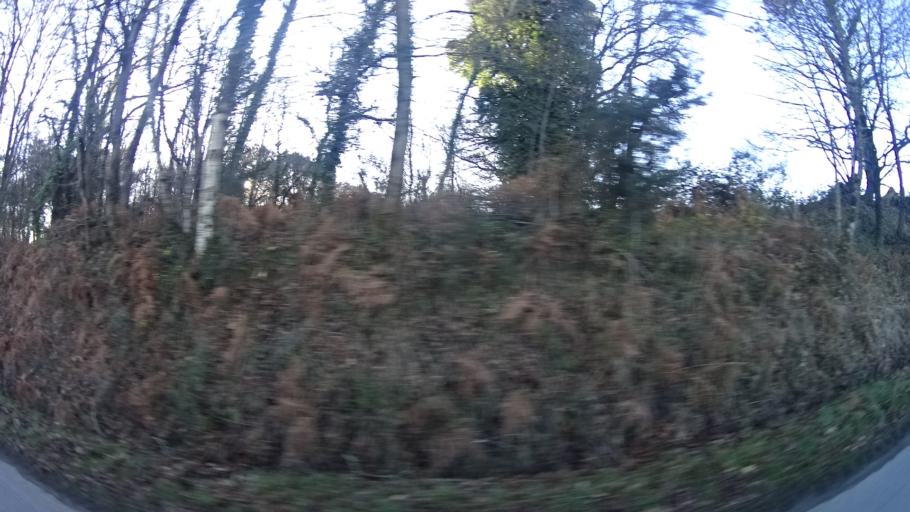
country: FR
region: Brittany
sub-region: Departement du Morbihan
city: Allaire
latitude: 47.6550
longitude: -2.1580
